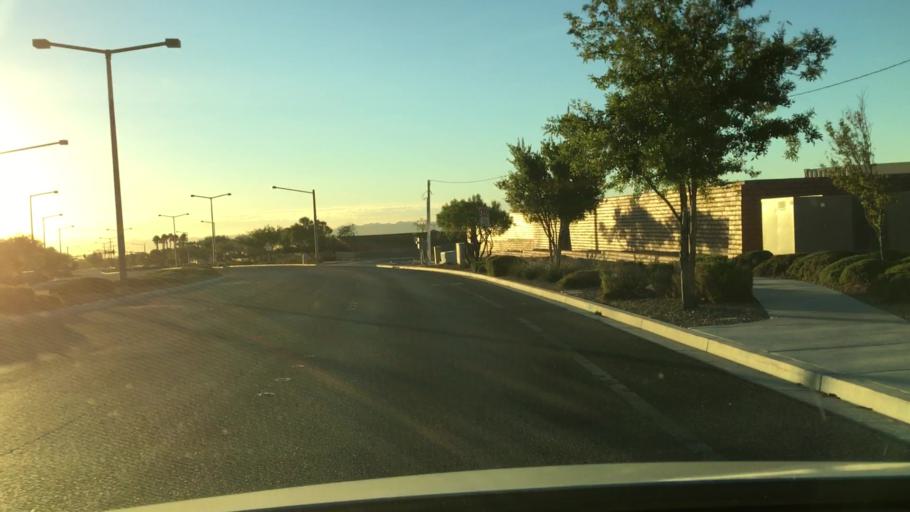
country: US
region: Nevada
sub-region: Clark County
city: Summerlin South
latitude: 36.1162
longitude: -115.3334
